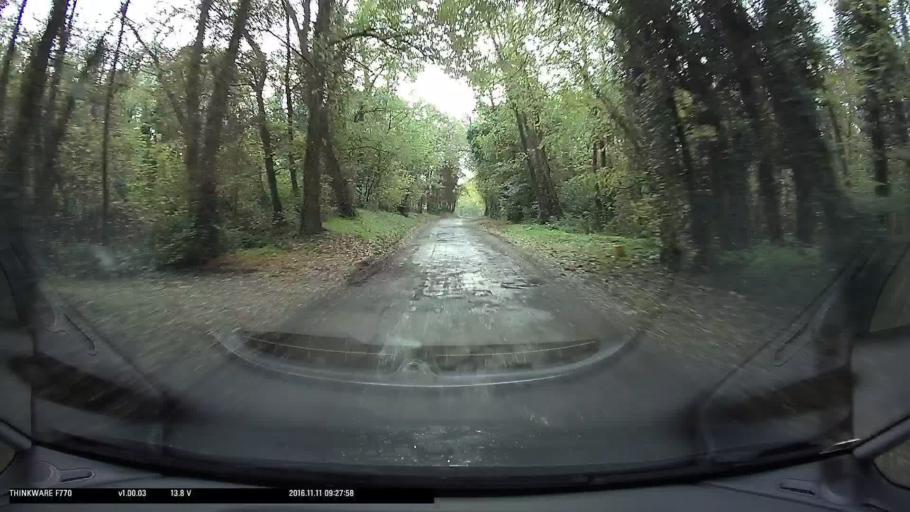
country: FR
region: Ile-de-France
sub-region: Departement du Val-d'Oise
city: Osny
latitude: 49.0726
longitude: 2.0399
